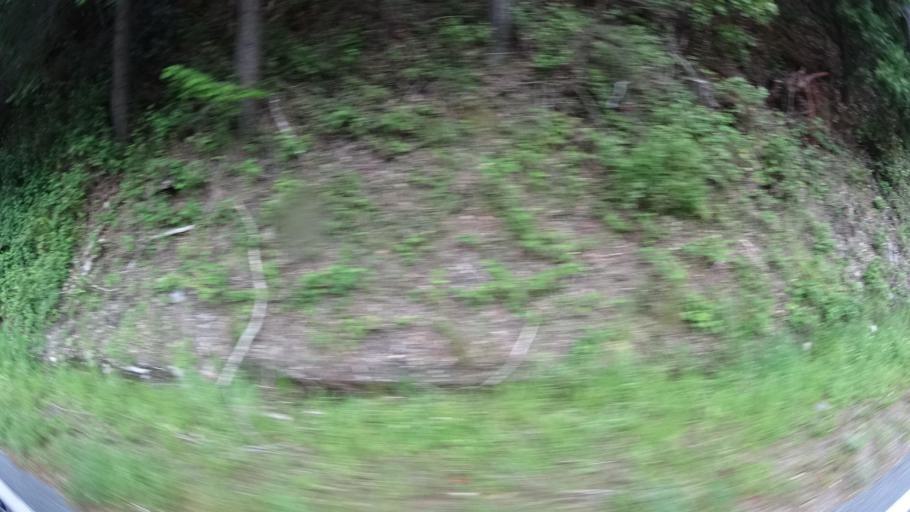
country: US
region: California
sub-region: Humboldt County
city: Willow Creek
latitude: 41.2547
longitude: -123.6329
